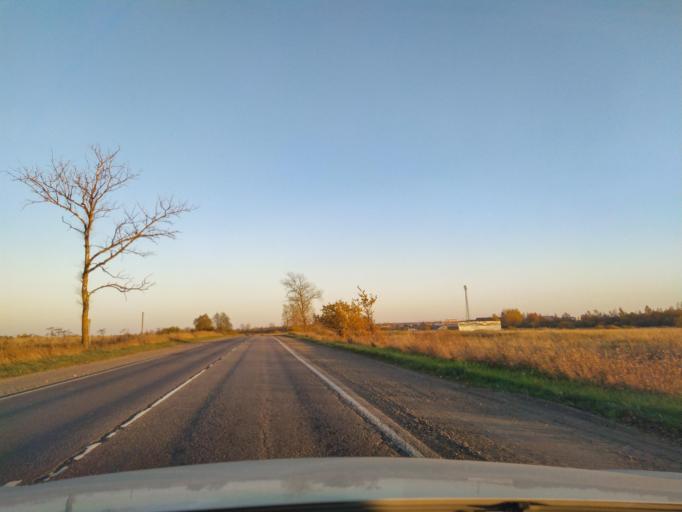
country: RU
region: Leningrad
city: Maloye Verevo
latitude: 59.6077
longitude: 30.2451
